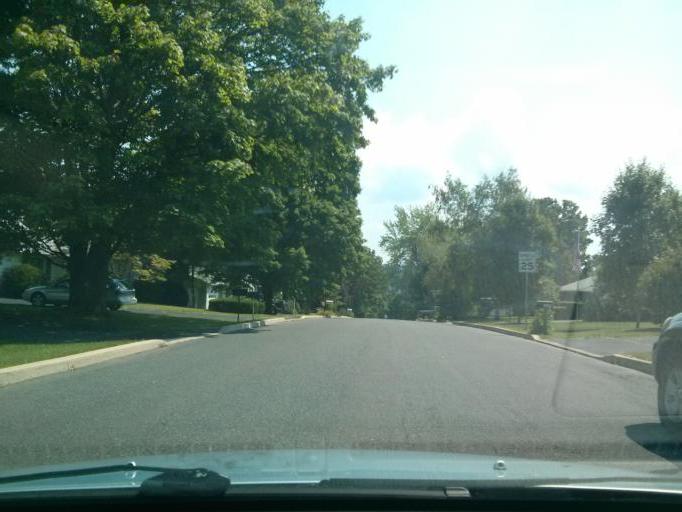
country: US
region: Pennsylvania
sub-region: Centre County
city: State College
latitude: 40.8070
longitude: -77.8847
